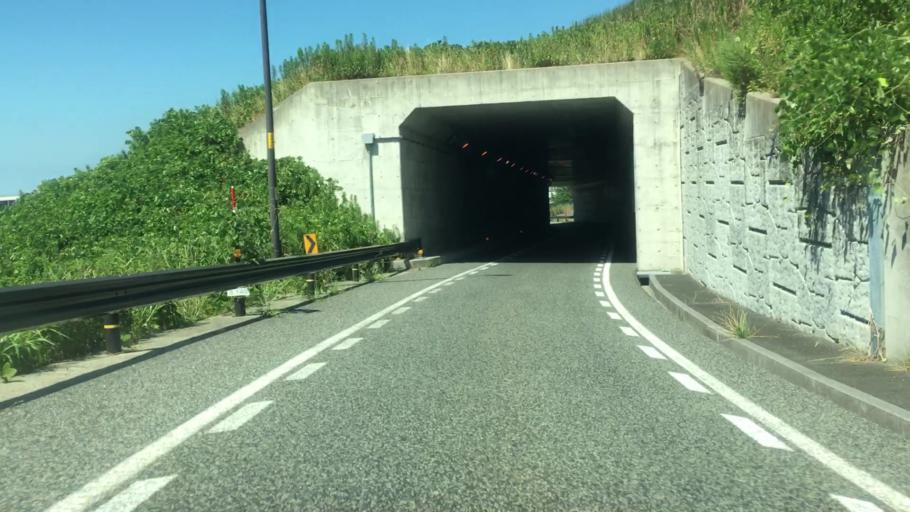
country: JP
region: Tottori
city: Tottori
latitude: 35.4227
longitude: 134.2067
